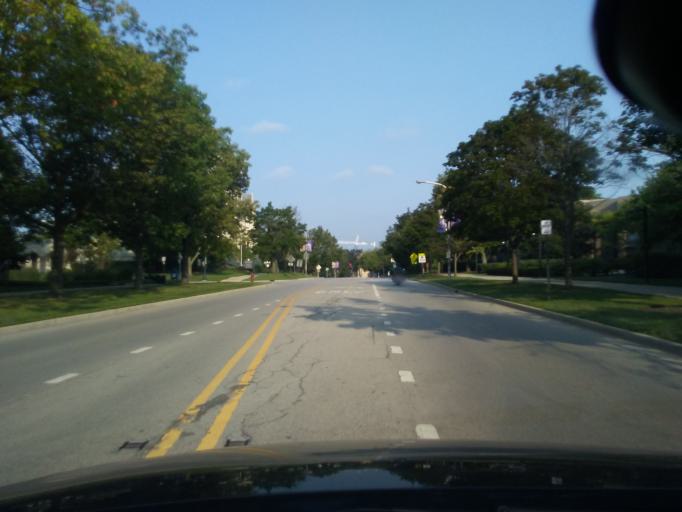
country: US
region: Illinois
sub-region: Cook County
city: Evanston
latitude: 42.0504
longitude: -87.6749
